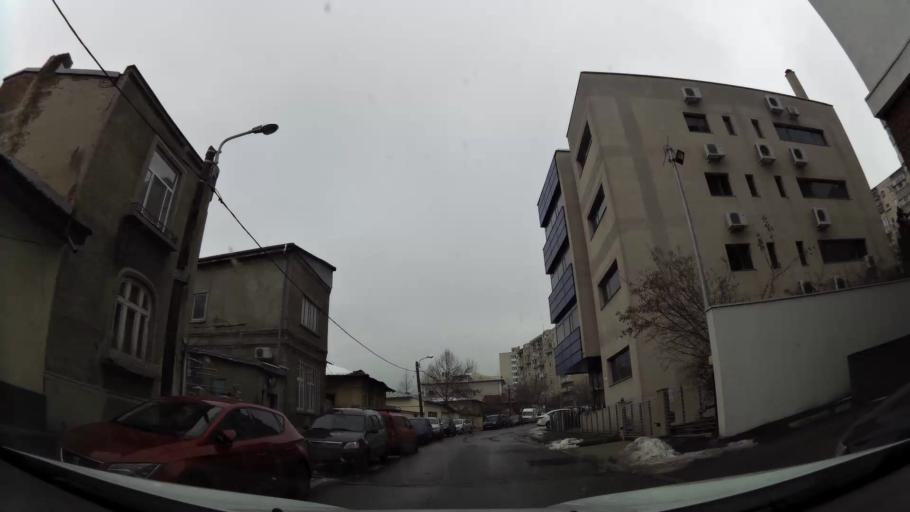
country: RO
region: Bucuresti
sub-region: Municipiul Bucuresti
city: Bucharest
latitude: 44.4181
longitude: 26.1180
